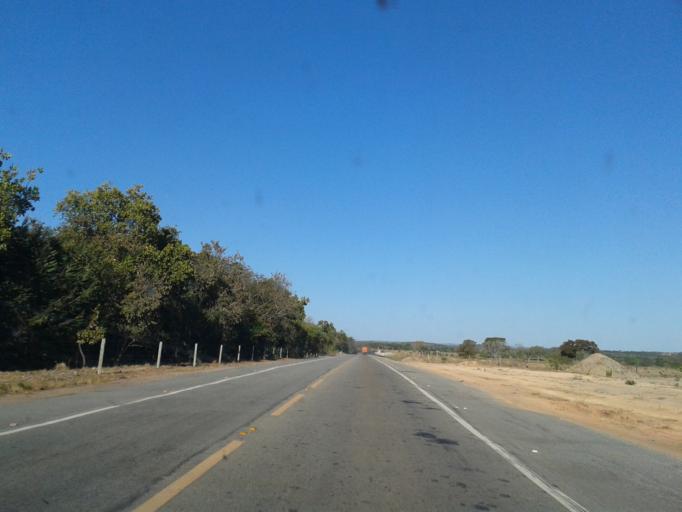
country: BR
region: Goias
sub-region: Itapirapua
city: Itapirapua
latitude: -15.2972
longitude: -50.4592
